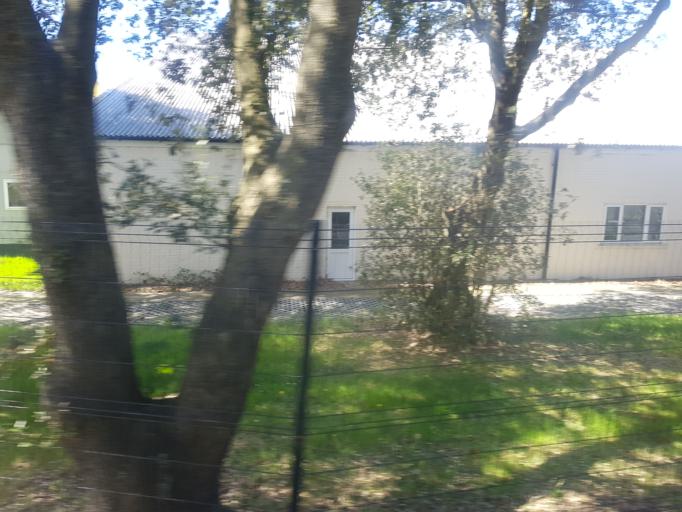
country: GB
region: England
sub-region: Isle of Wight
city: East Cowes
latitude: 50.7433
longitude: -1.2715
